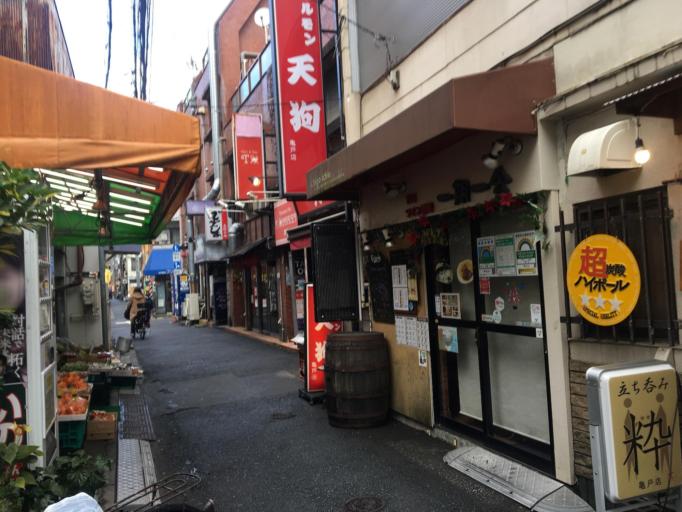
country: JP
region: Tokyo
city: Urayasu
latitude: 35.6992
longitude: 139.8261
